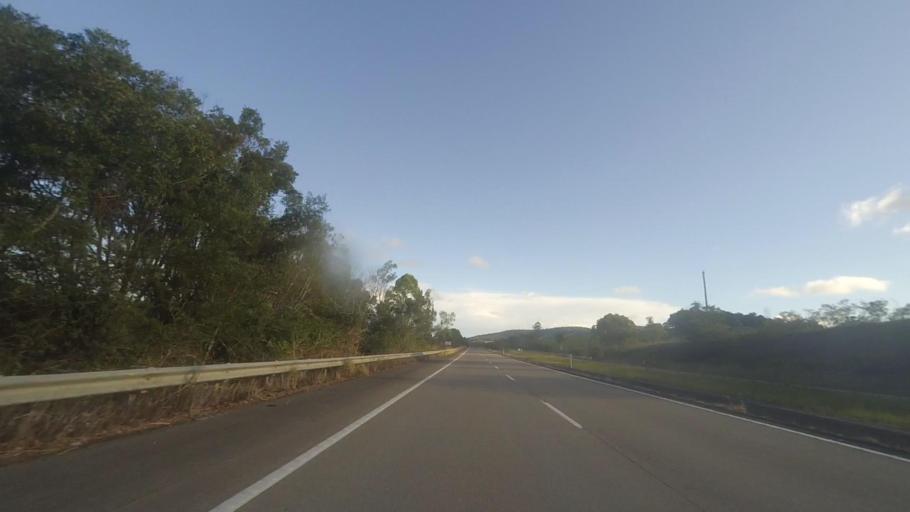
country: AU
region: New South Wales
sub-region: Great Lakes
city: Nabiac
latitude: -32.2550
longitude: 152.3242
